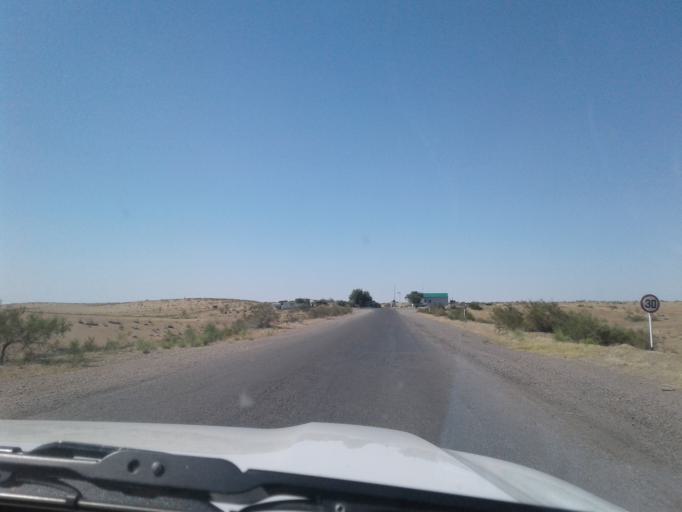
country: TM
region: Mary
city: Serhetabat
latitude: 35.9866
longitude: 62.6270
